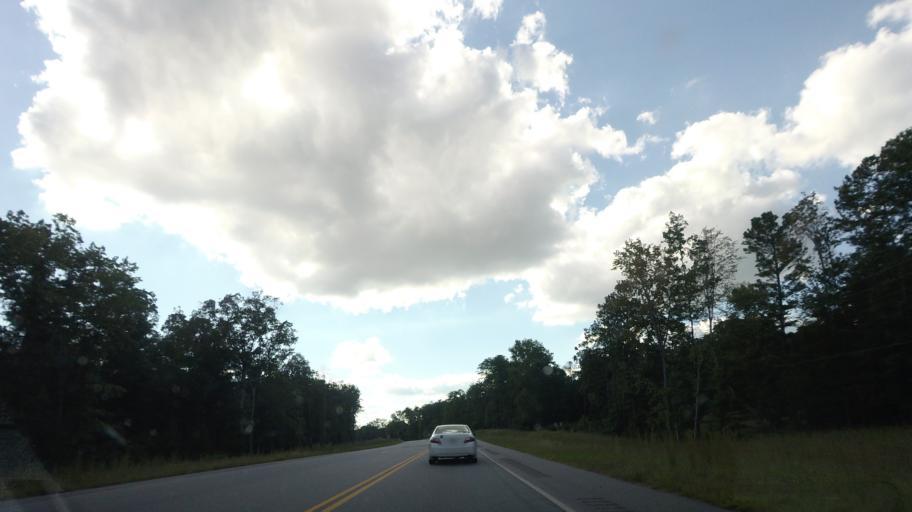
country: US
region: Georgia
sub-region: Lamar County
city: Barnesville
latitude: 33.0561
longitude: -84.0587
